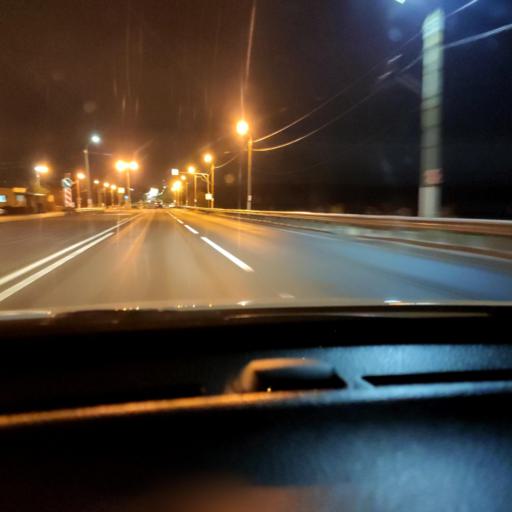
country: RU
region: Voronezj
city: Pridonskoy
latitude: 51.6504
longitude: 39.0729
